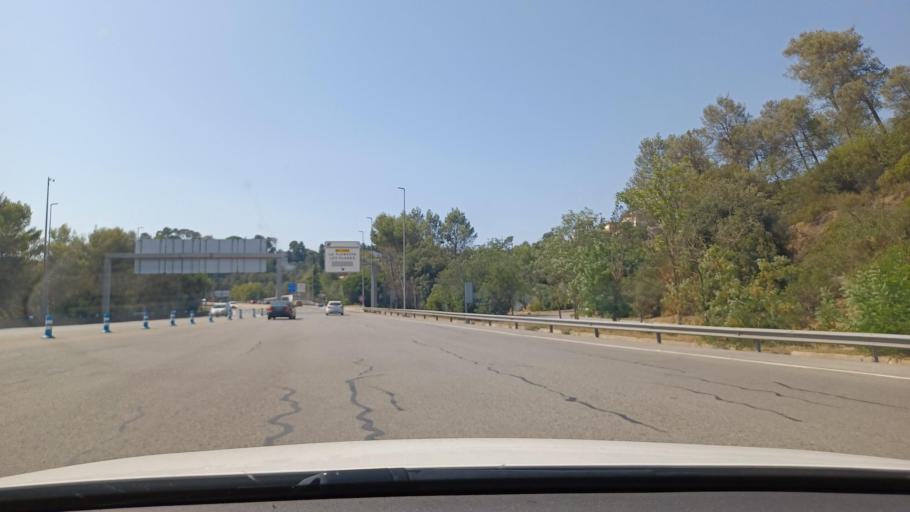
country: ES
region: Catalonia
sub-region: Provincia de Barcelona
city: Sant Cugat del Valles
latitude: 41.4379
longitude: 2.0751
